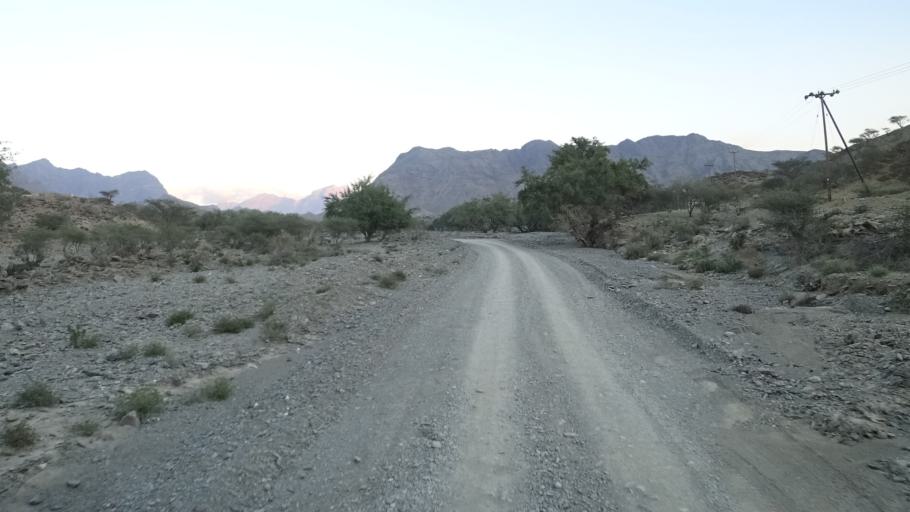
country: OM
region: Al Batinah
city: Rustaq
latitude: 23.2794
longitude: 57.3538
